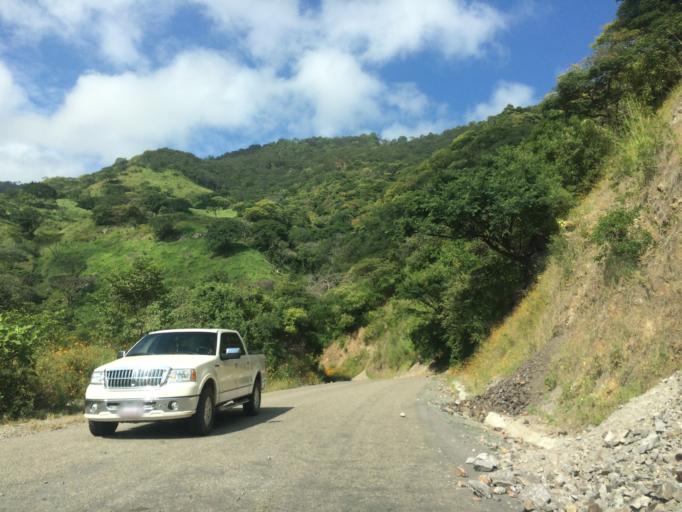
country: MX
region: Nayarit
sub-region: Ahuacatlan
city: Ahuacatlan
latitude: 21.0040
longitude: -104.4834
